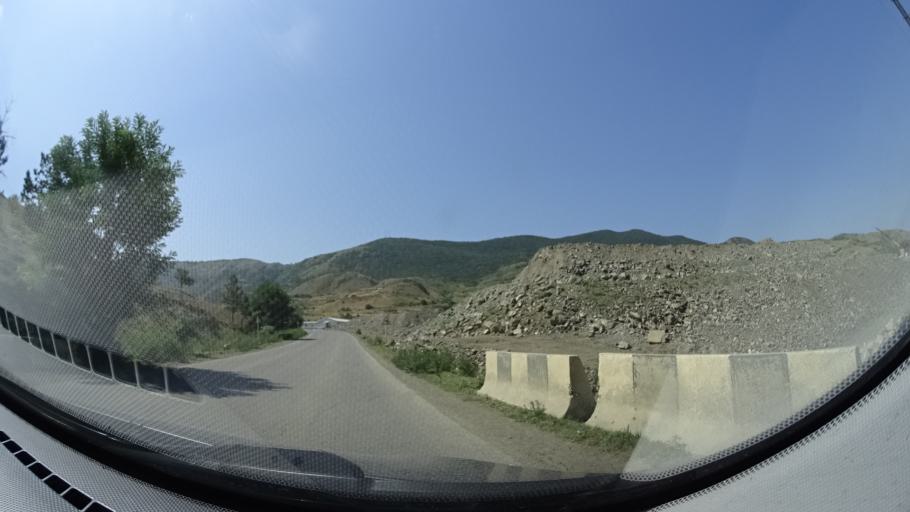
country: GE
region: Samtskhe-Javakheti
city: Aspindza
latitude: 41.6044
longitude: 43.1470
